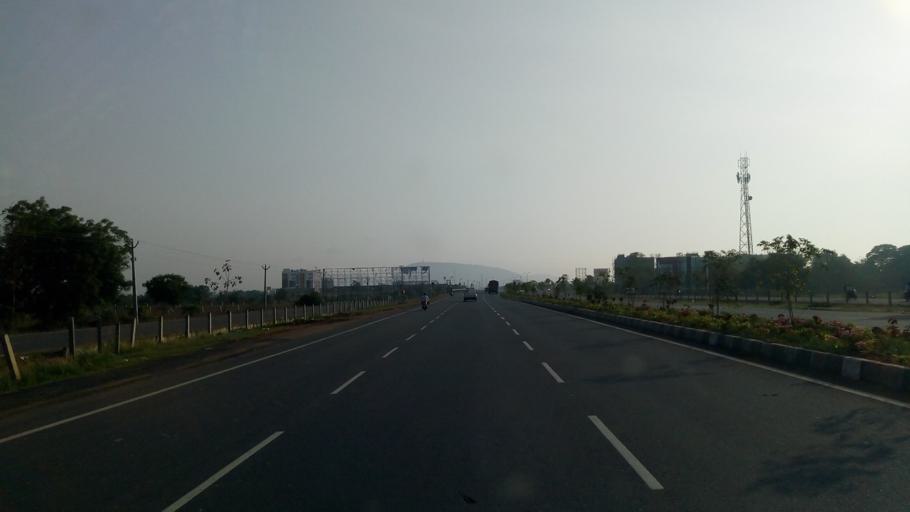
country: IN
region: Andhra Pradesh
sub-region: Guntur
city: Mangalagiri
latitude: 16.3991
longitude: 80.5498
